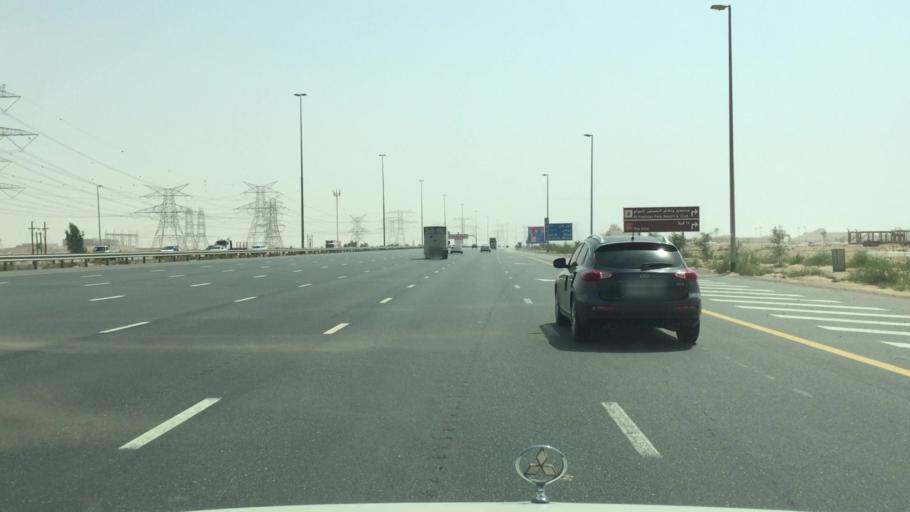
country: AE
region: Dubai
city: Dubai
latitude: 25.0799
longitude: 55.3812
